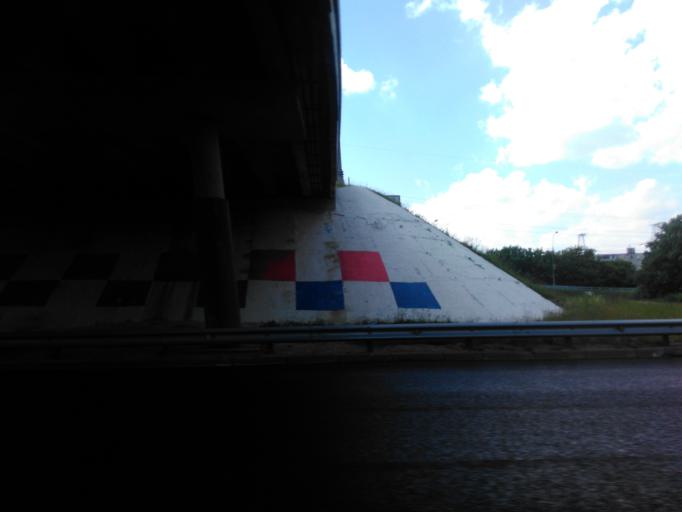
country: RU
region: Moskovskaya
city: Kuskovo
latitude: 55.7188
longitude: 37.8389
